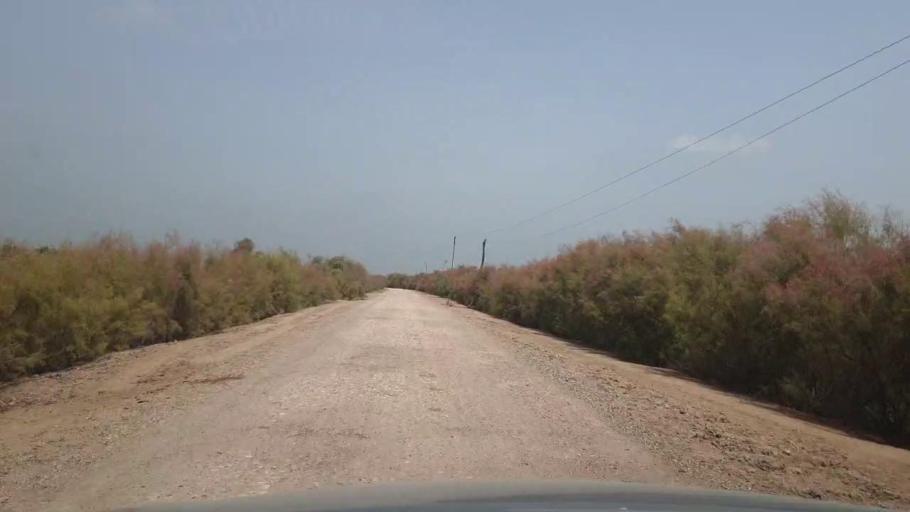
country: PK
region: Sindh
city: Garhi Yasin
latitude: 27.9549
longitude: 68.3654
